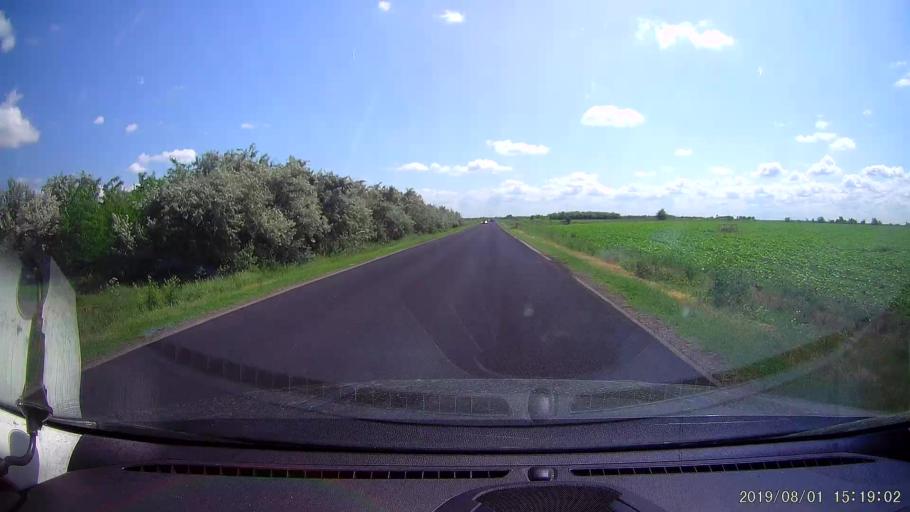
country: RO
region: Braila
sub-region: Comuna Unirea
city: Unirea
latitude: 45.0966
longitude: 27.8160
